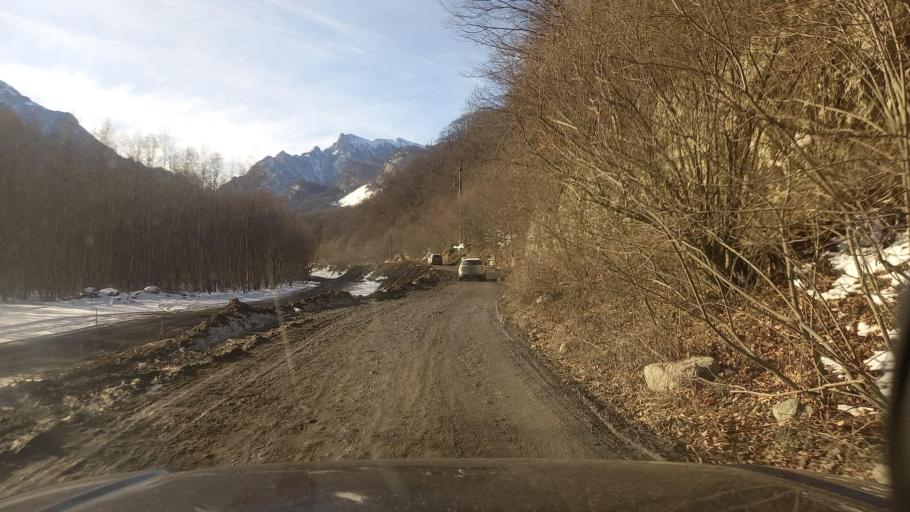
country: RU
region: North Ossetia
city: Gizel'
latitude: 42.9269
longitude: 44.5419
